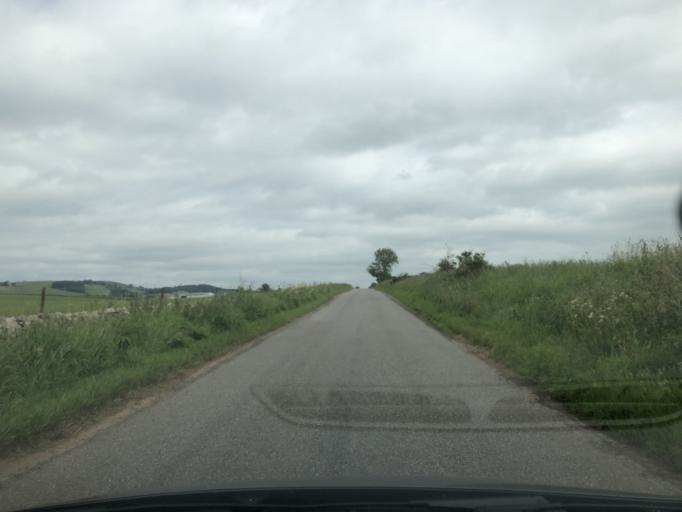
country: GB
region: Scotland
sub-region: Angus
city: Forfar
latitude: 56.7264
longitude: -2.9097
